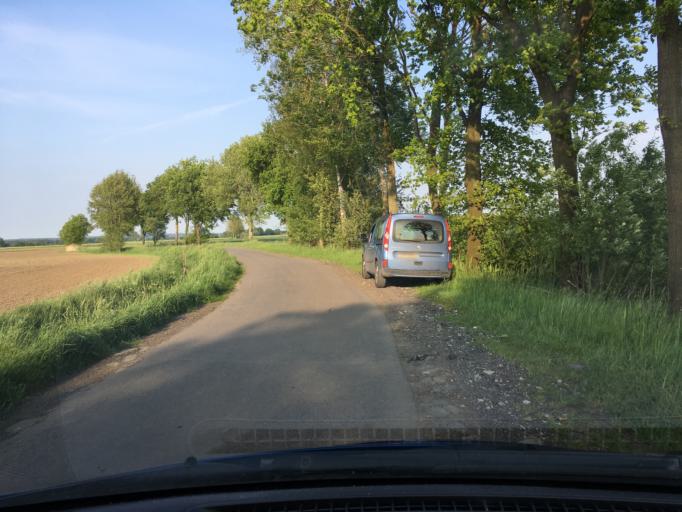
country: DE
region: Lower Saxony
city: Handorf
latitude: 53.3628
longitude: 10.3613
